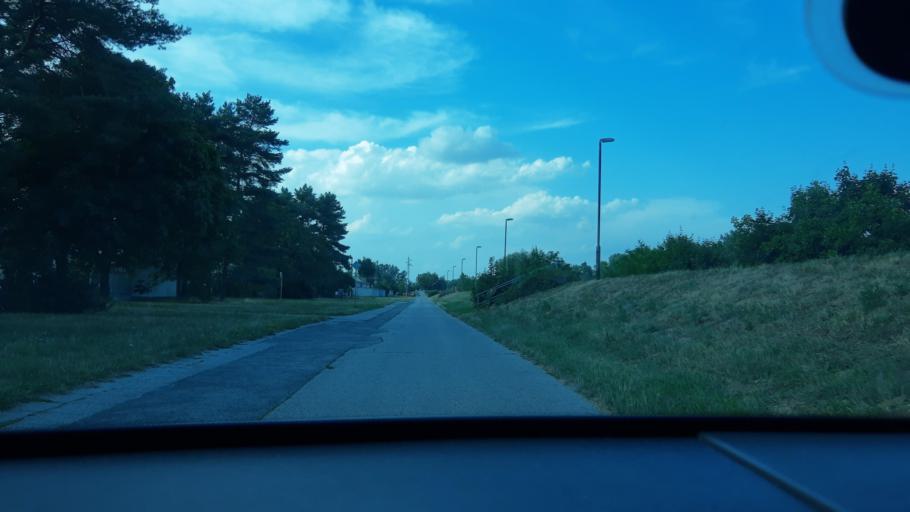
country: SK
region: Trnavsky
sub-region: Okres Trnava
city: Piestany
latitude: 48.6014
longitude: 17.8405
